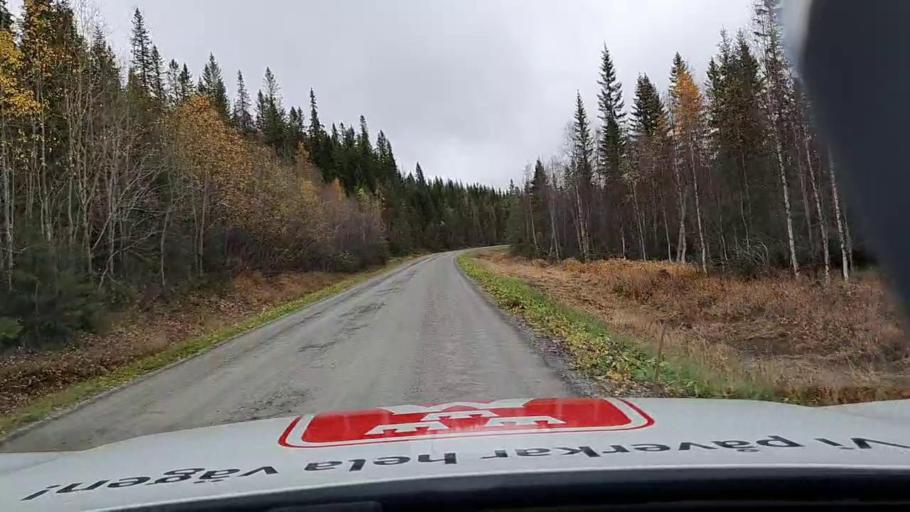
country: SE
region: Jaemtland
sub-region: Krokoms Kommun
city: Valla
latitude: 63.0430
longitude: 13.9613
